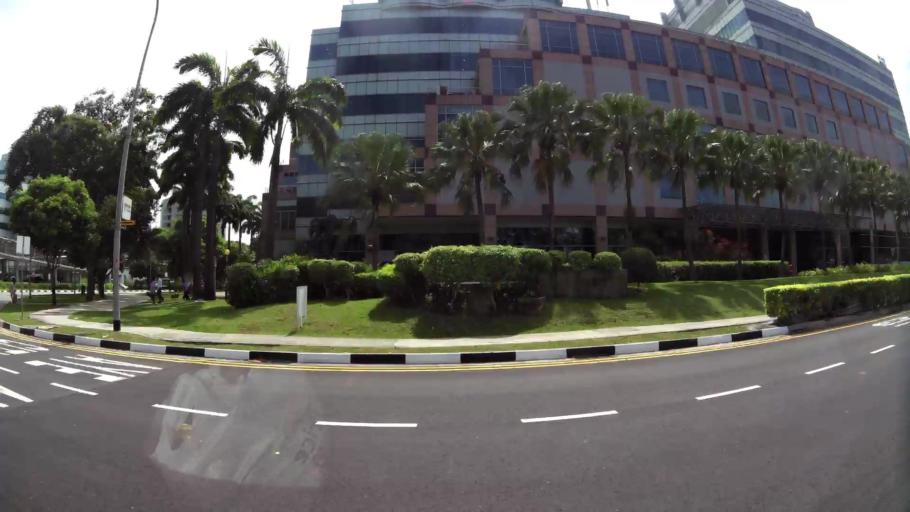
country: SG
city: Singapore
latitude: 1.3294
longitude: 103.7453
